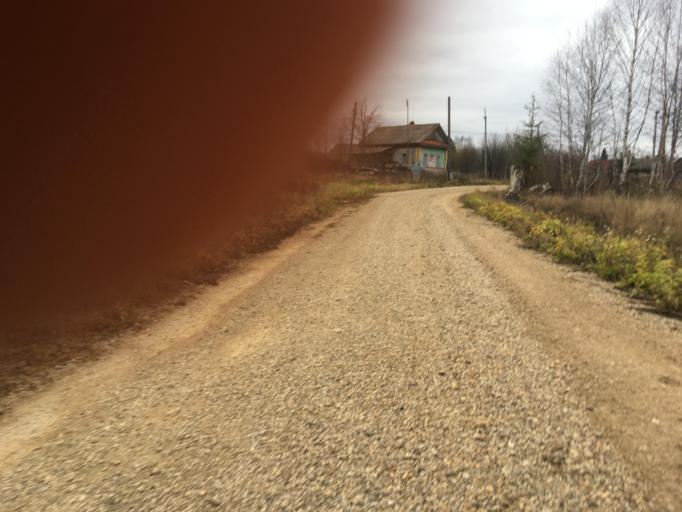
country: RU
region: Perm
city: Komarikhinskiy
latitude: 58.0886
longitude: 57.1122
